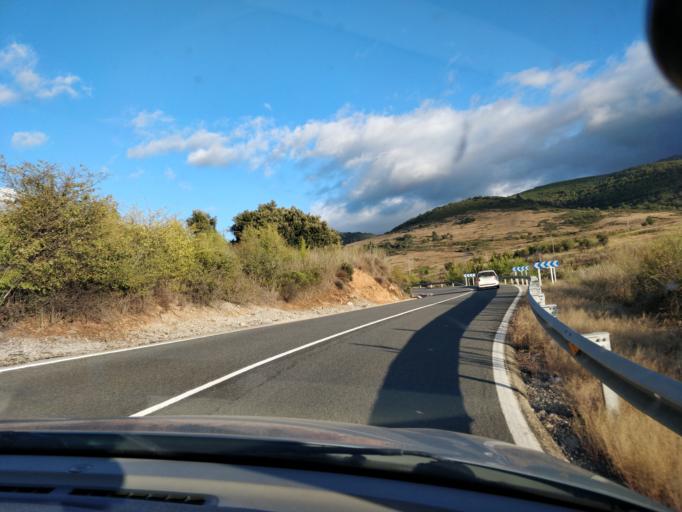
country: ES
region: Castille and Leon
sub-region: Provincia de Leon
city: Borrenes
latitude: 42.4925
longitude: -6.7068
